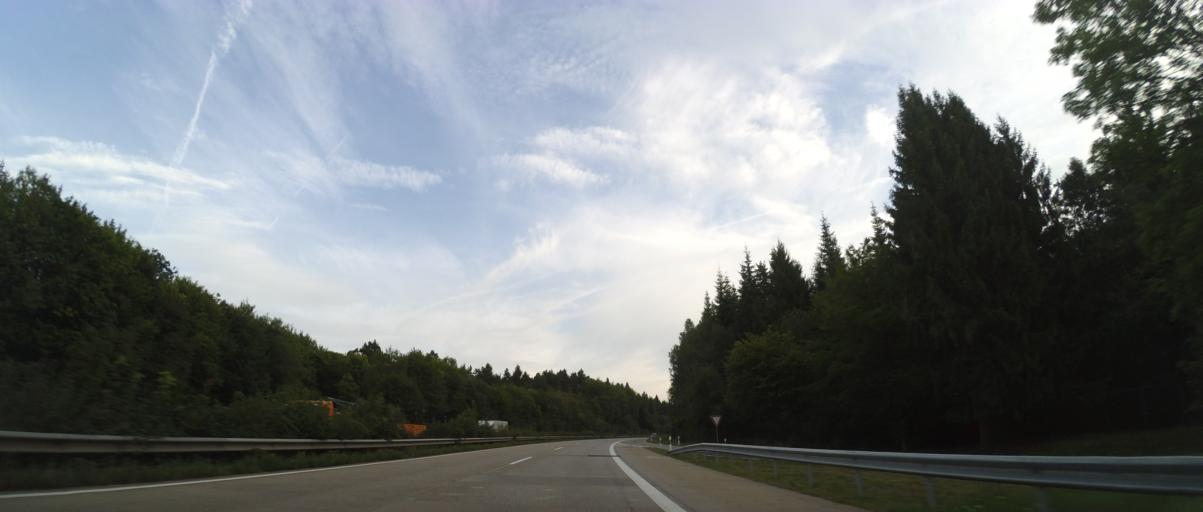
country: DE
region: Rheinland-Pfalz
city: Greimerath
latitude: 50.0320
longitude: 6.9146
